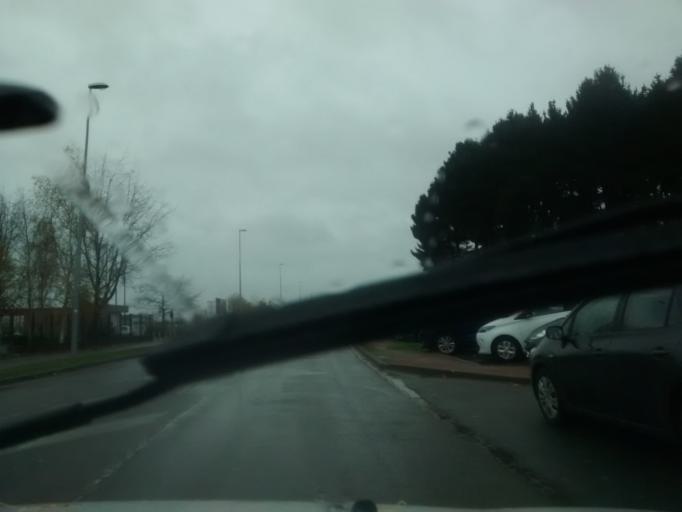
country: FR
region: Brittany
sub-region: Departement d'Ille-et-Vilaine
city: Cesson-Sevigne
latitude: 48.1275
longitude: -1.6261
